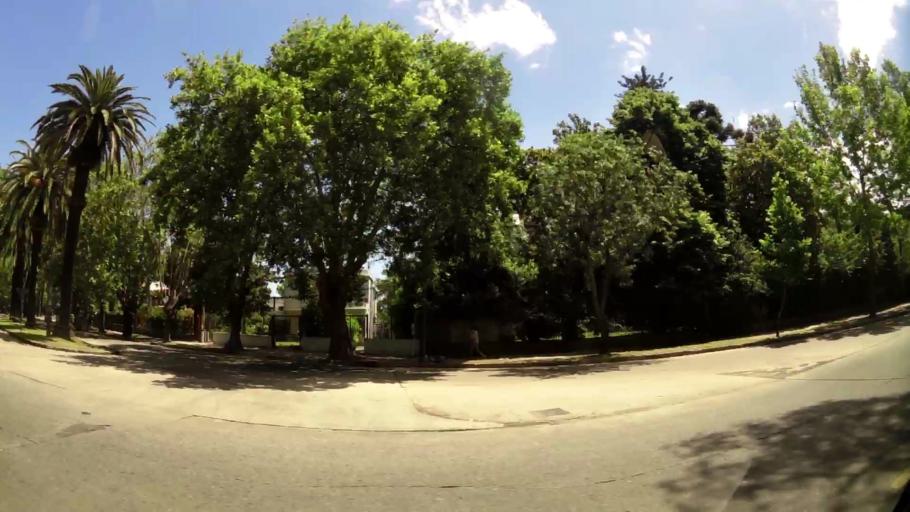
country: UY
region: Montevideo
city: Montevideo
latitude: -34.8635
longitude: -56.1962
